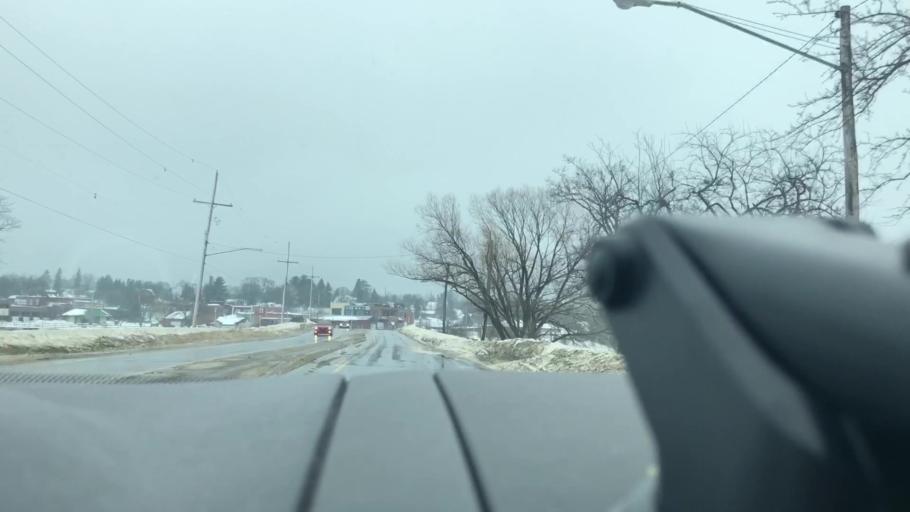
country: US
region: Michigan
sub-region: Charlevoix County
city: East Jordan
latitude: 45.1530
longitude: -85.1314
